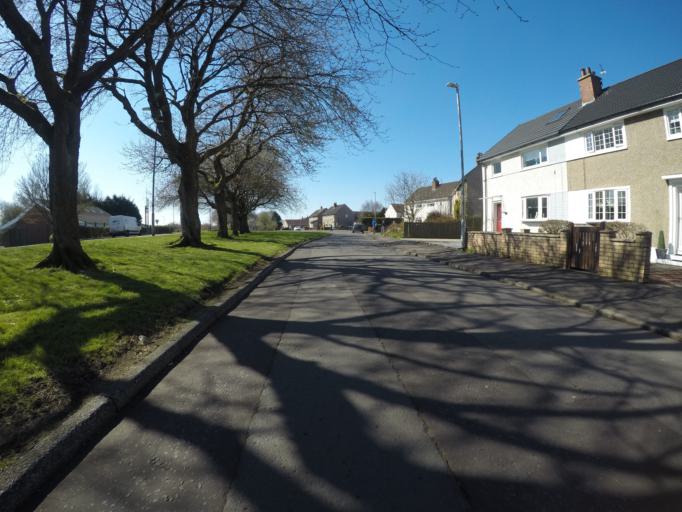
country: GB
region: Scotland
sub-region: North Ayrshire
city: Irvine
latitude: 55.6227
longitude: -4.6526
